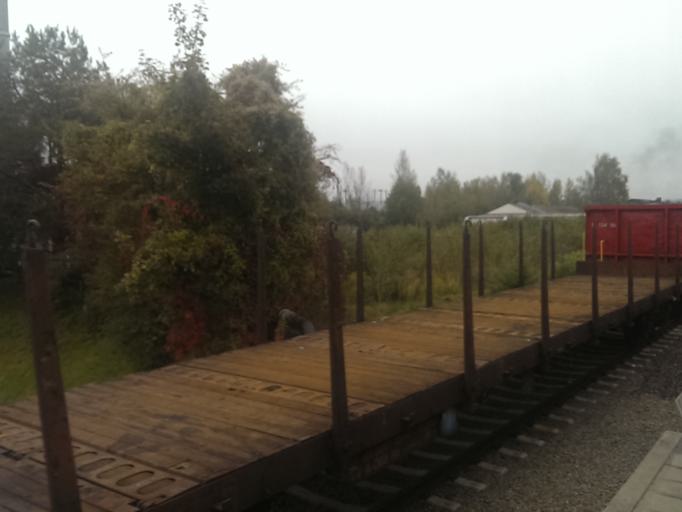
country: AT
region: Upper Austria
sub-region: Linz Stadt
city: Linz
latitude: 48.2649
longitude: 14.3189
